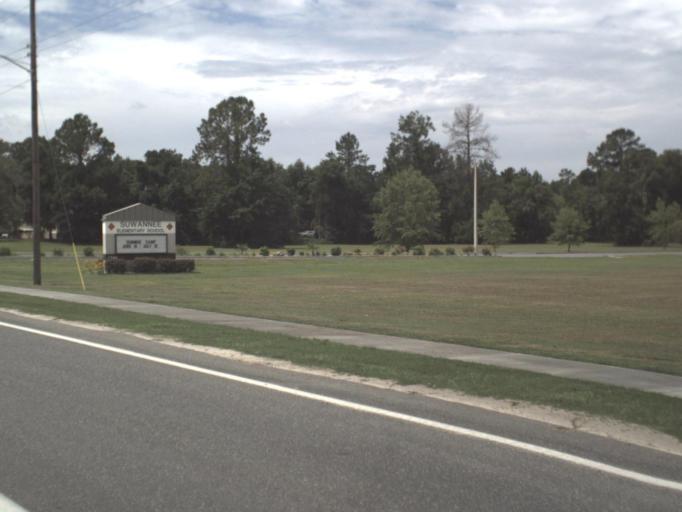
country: US
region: Florida
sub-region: Suwannee County
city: Live Oak
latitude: 30.2779
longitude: -82.9878
